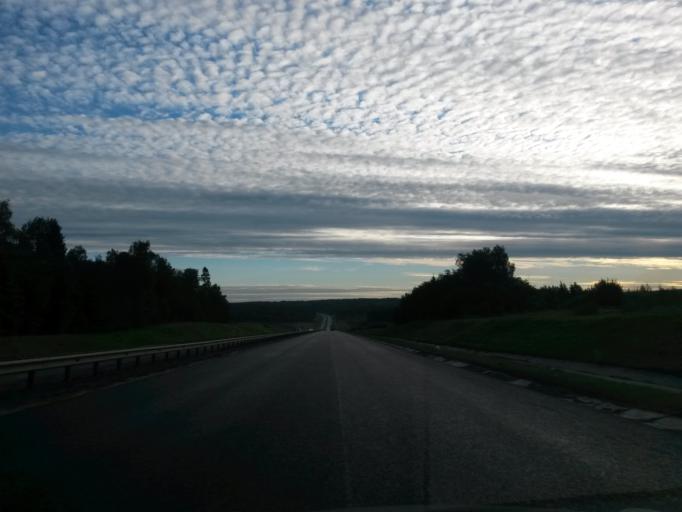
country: RU
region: Vladimir
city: Strunino
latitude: 56.5294
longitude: 38.5733
